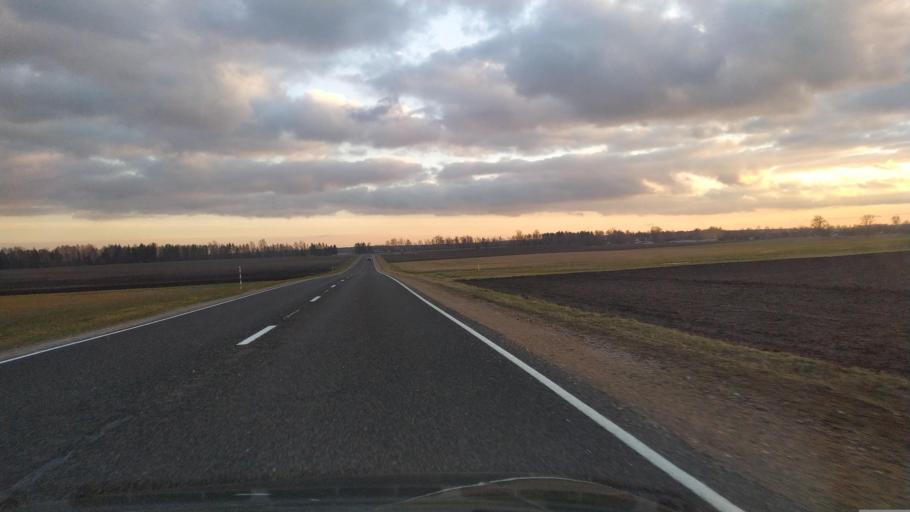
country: BY
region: Brest
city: Kamyanyets
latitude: 52.3786
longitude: 23.7897
